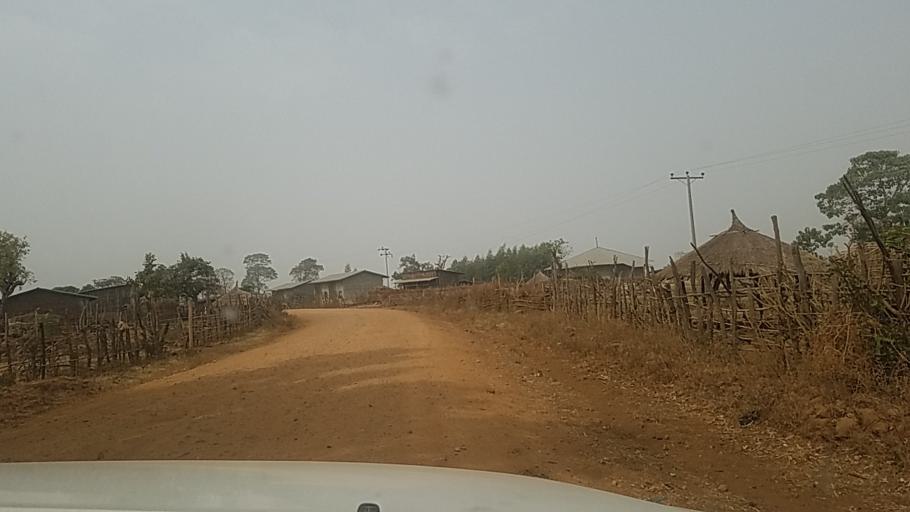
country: ET
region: Amhara
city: Bure
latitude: 10.8288
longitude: 36.3304
